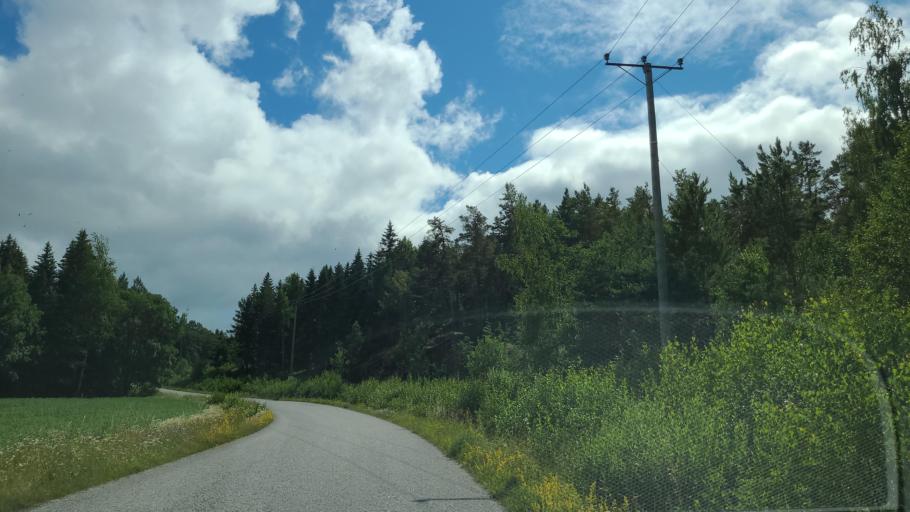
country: FI
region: Varsinais-Suomi
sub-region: Aboland-Turunmaa
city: Nagu
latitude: 60.1832
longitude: 22.0202
